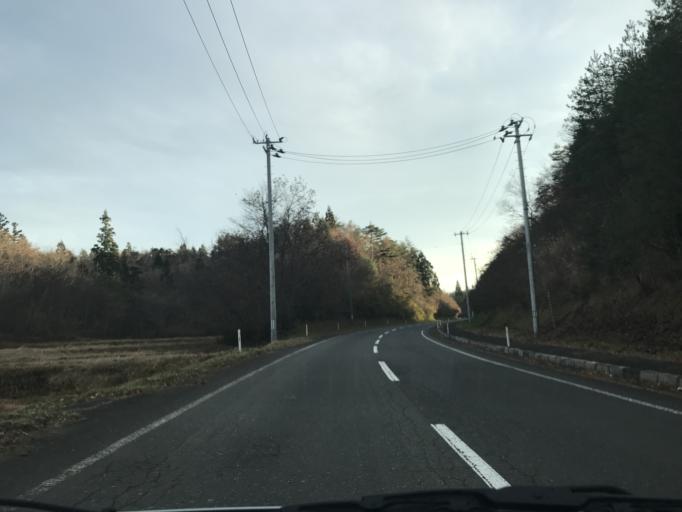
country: JP
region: Iwate
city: Ichinoseki
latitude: 38.9871
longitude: 141.0677
